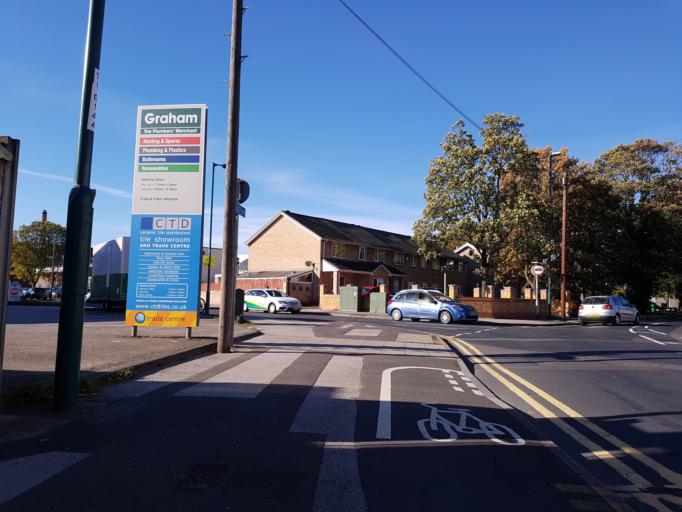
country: GB
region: England
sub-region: Nottingham
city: Nottingham
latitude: 52.9444
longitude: -1.1795
